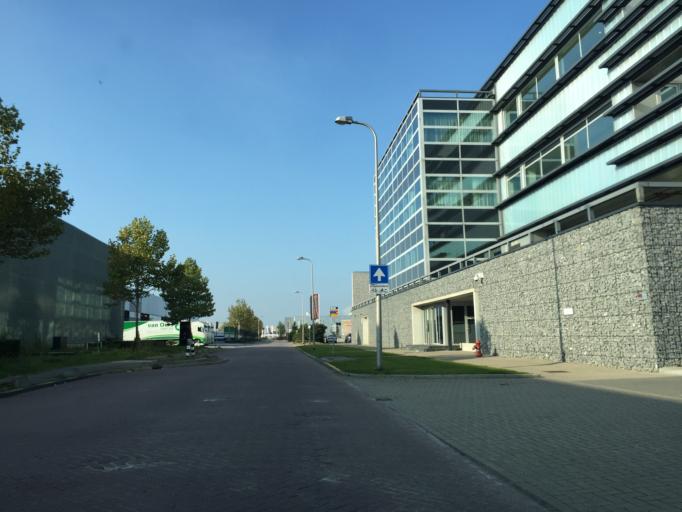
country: NL
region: South Holland
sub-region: Gemeente Zwijndrecht
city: Heerjansdam
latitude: 51.8579
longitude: 4.5636
